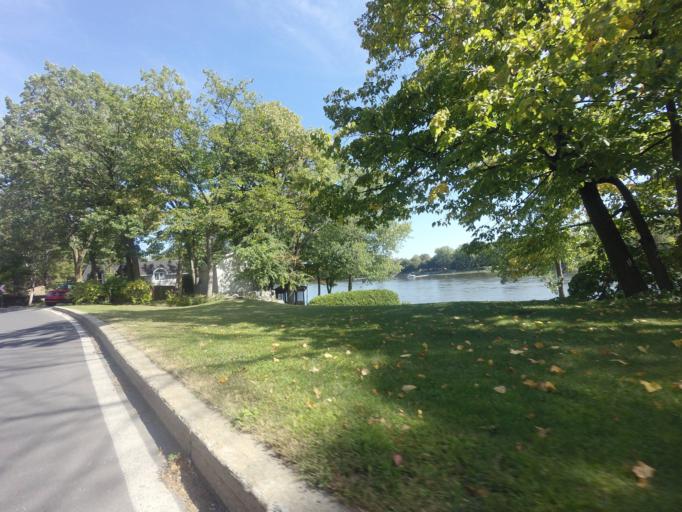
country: CA
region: Quebec
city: Dollard-Des Ormeaux
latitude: 45.5092
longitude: -73.8583
